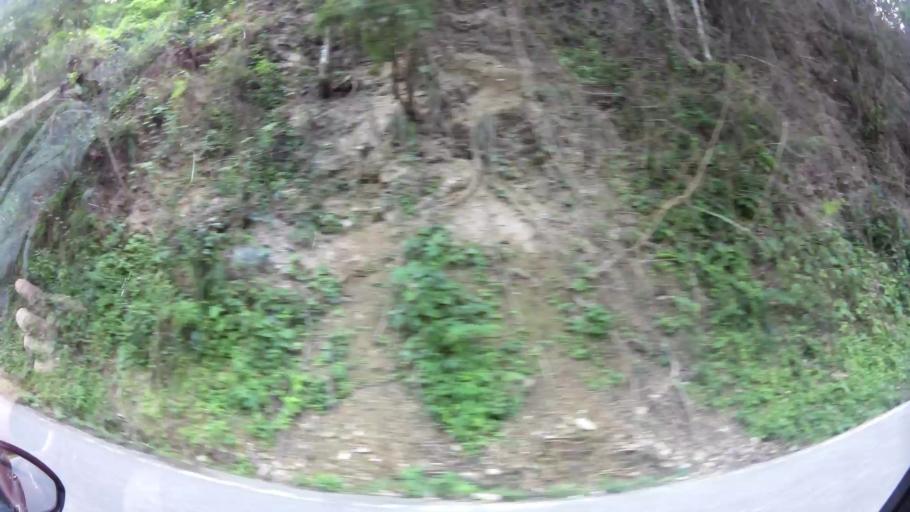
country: TT
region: Diego Martin
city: Petit Valley
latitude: 10.7258
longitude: -61.4937
